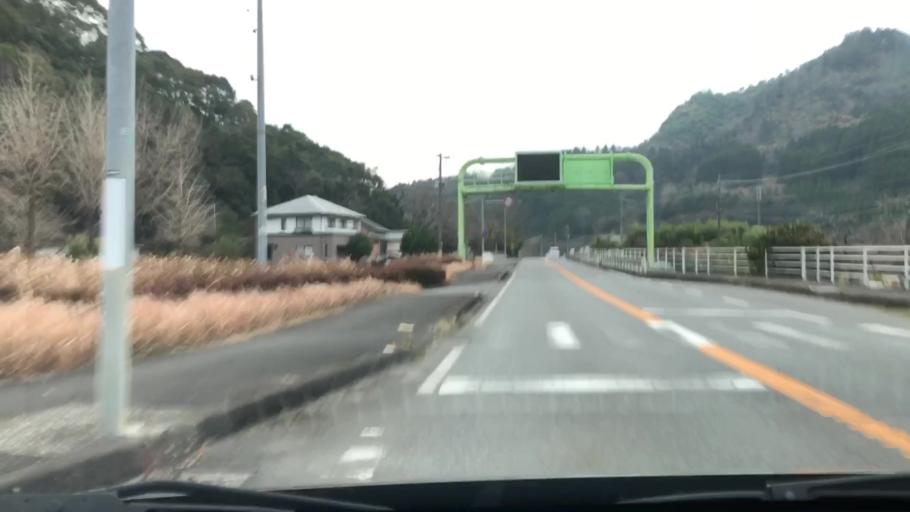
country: JP
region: Oita
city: Saiki
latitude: 32.9878
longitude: 131.8376
